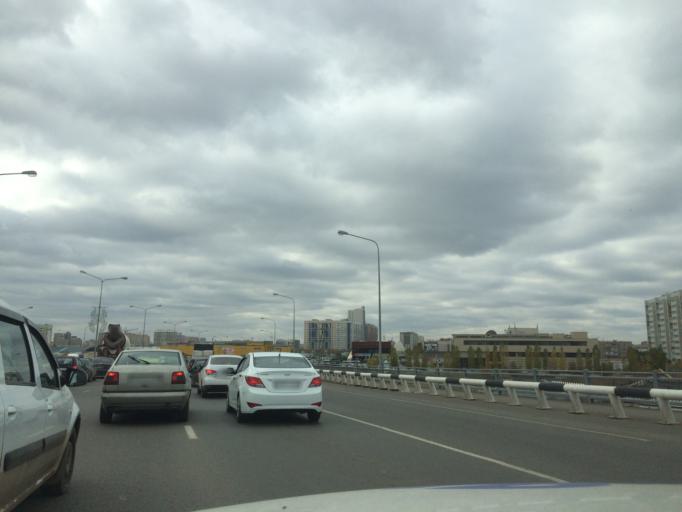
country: KZ
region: Astana Qalasy
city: Astana
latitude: 51.1802
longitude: 71.4417
